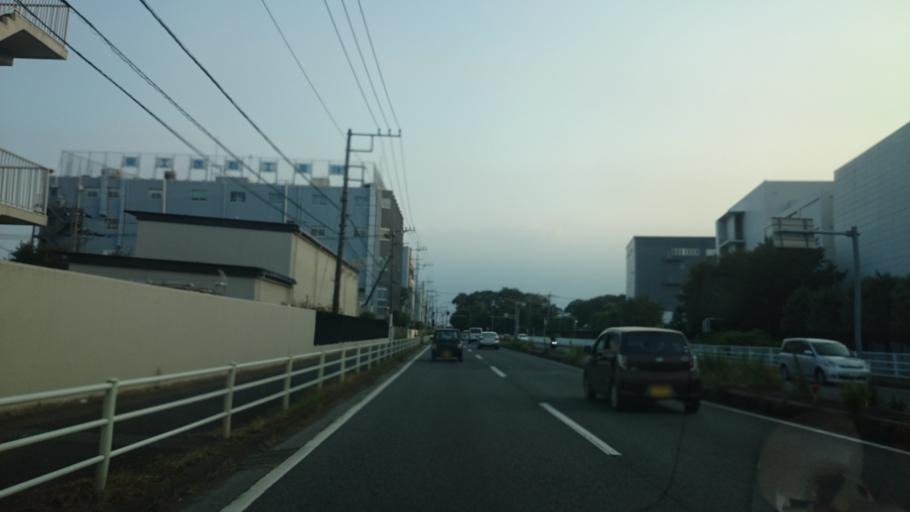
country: JP
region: Saitama
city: Kasukabe
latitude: 35.9793
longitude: 139.7374
